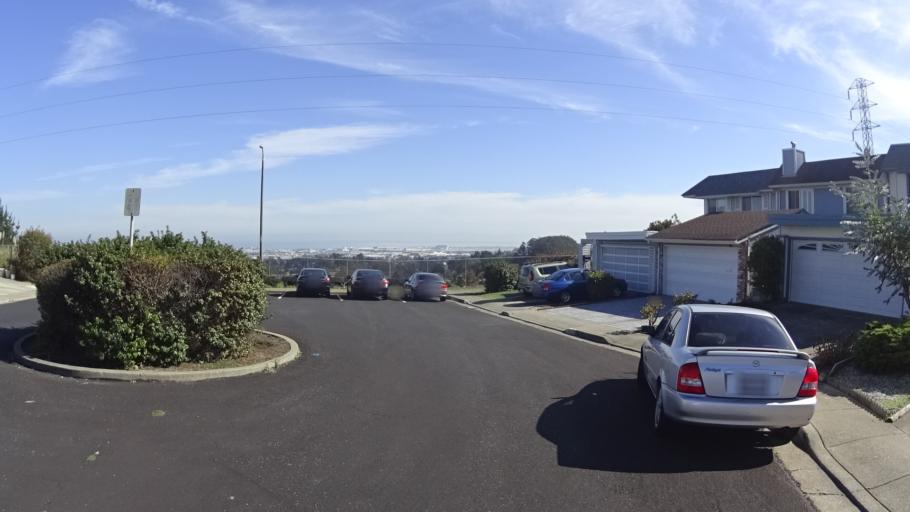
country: US
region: California
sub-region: San Mateo County
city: Colma
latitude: 37.6457
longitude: -122.4553
